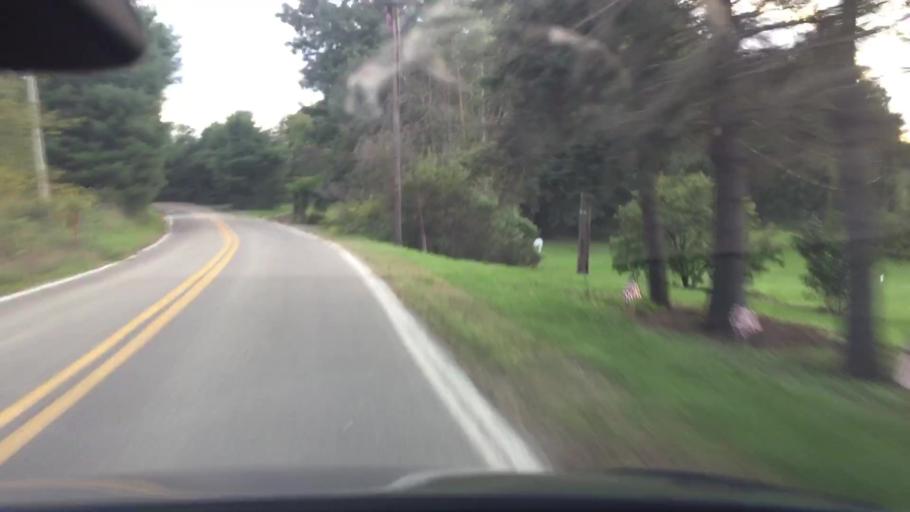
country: US
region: Pennsylvania
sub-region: Allegheny County
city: Curtisville
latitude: 40.6720
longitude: -79.8890
